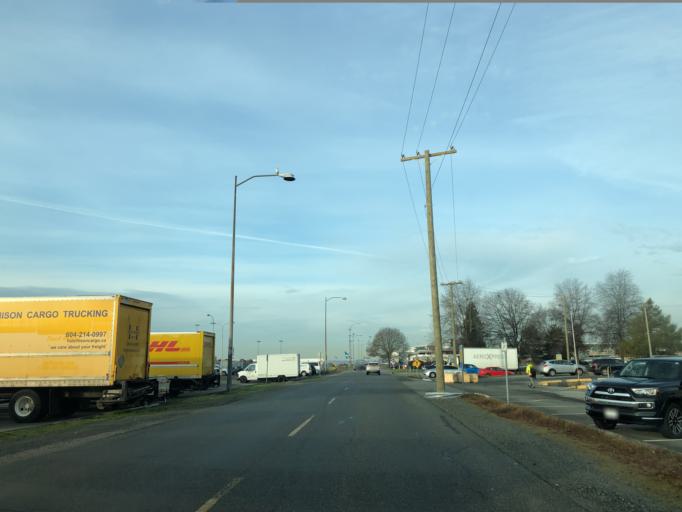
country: CA
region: British Columbia
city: Richmond
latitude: 49.1910
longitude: -123.1734
